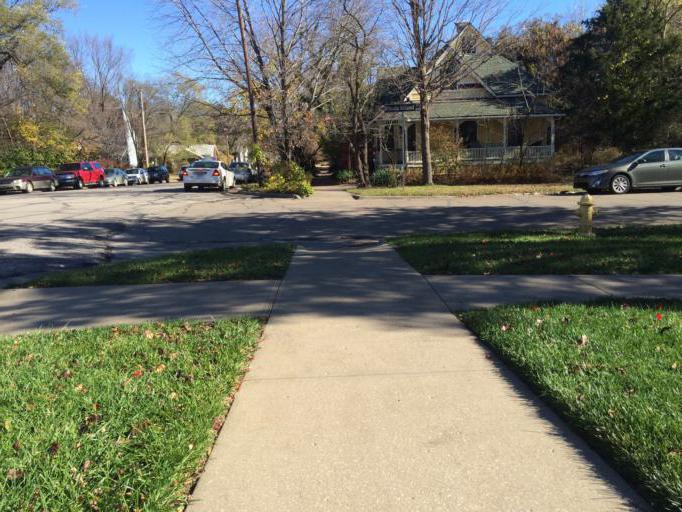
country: US
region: Kansas
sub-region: Douglas County
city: Lawrence
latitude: 38.9693
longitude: -95.2337
